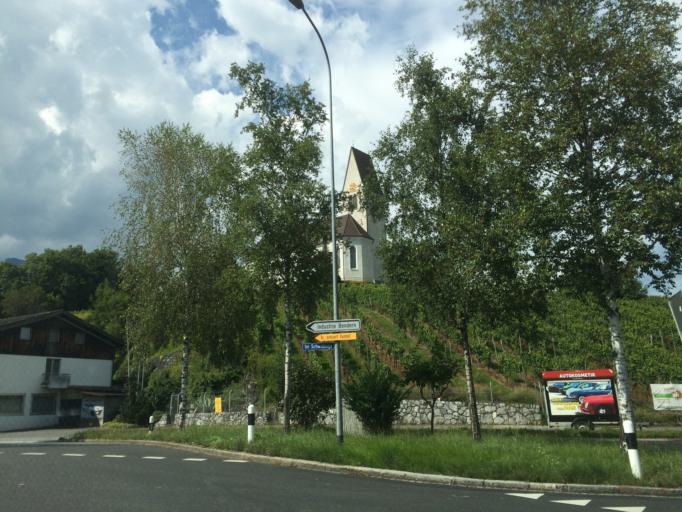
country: LI
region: Gamprin
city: Gamprin
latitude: 47.2104
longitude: 9.5045
